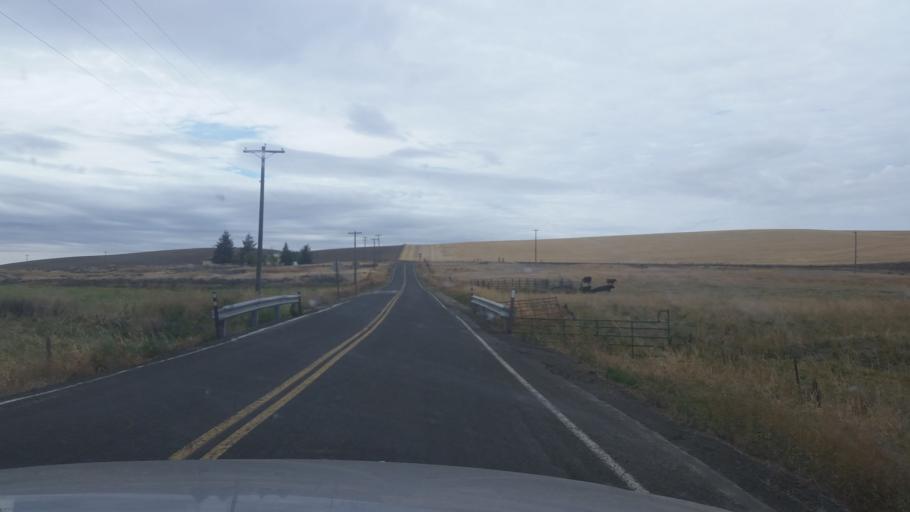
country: US
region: Washington
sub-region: Spokane County
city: Medical Lake
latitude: 47.5215
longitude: -117.9203
